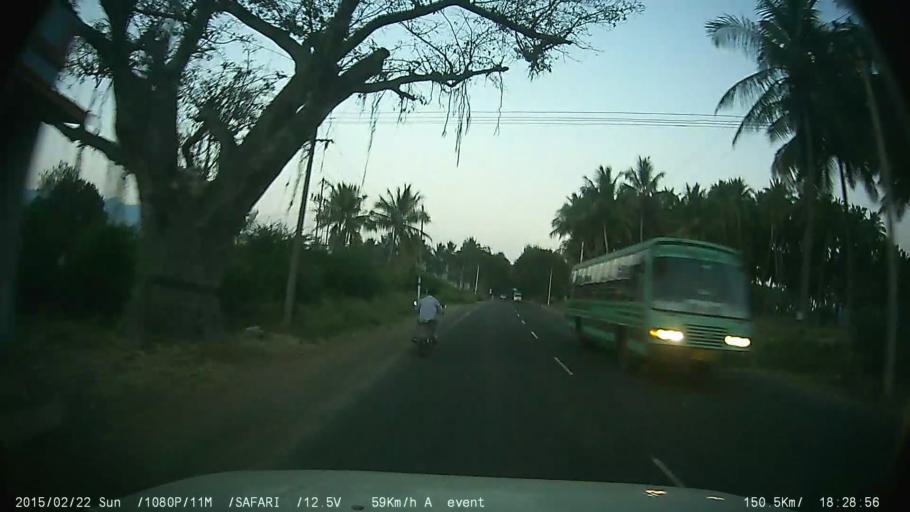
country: IN
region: Tamil Nadu
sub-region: Theni
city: Teni
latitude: 9.9811
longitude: 77.4516
